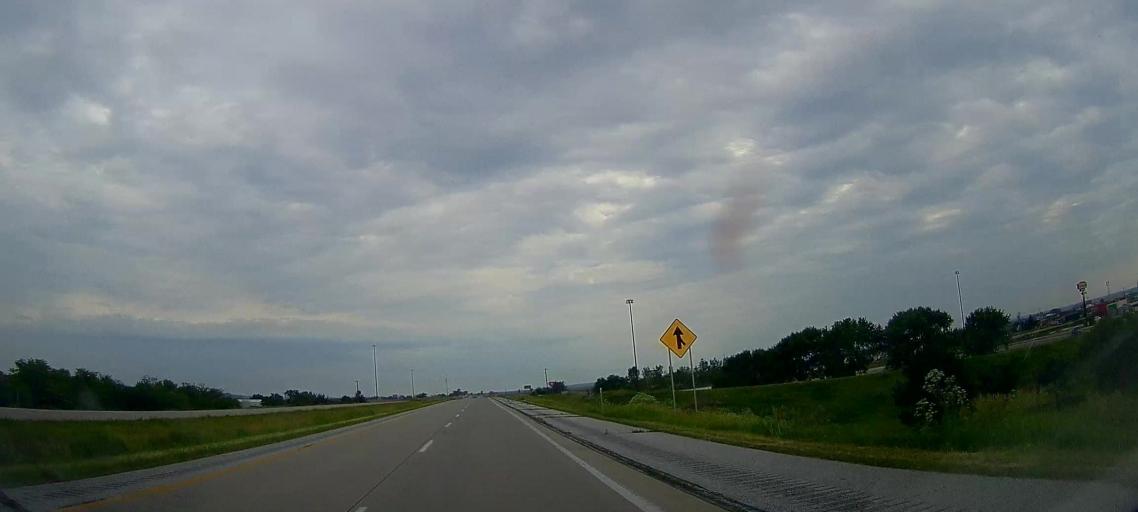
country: US
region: Iowa
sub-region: Harrison County
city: Missouri Valley
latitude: 41.5519
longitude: -95.9177
